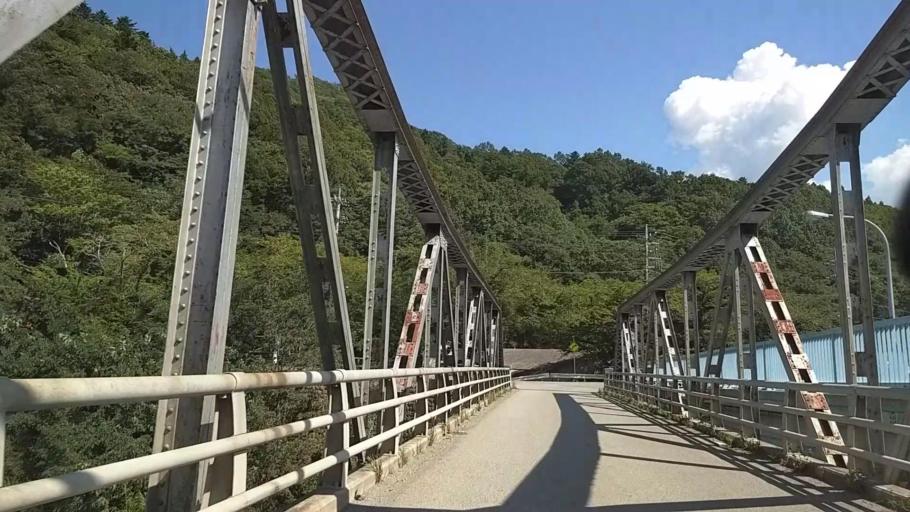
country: JP
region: Yamanashi
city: Ryuo
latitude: 35.4653
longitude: 138.4428
